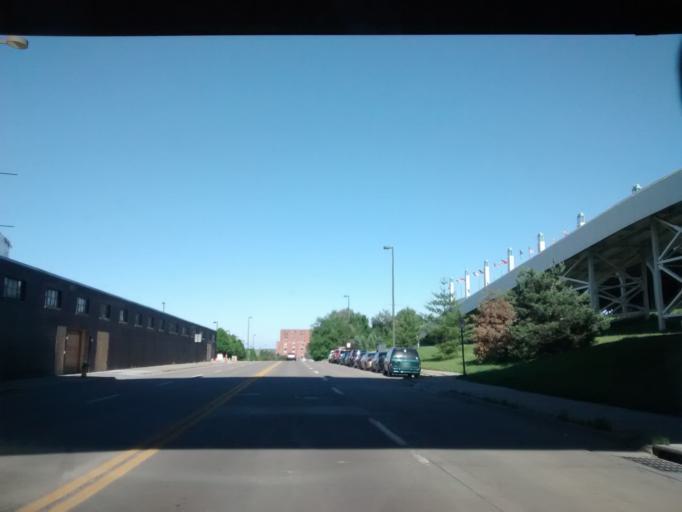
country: US
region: Nebraska
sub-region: Douglas County
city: Omaha
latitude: 41.2523
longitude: -95.9294
